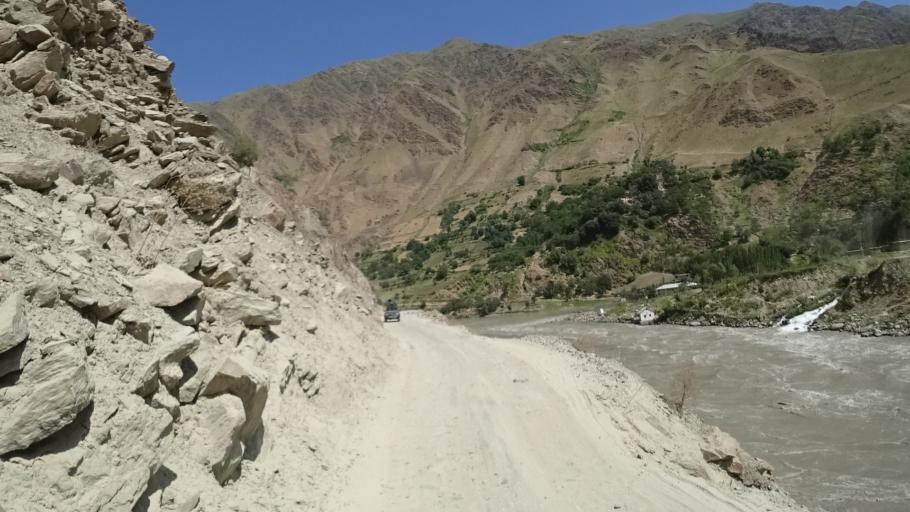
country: AF
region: Badakhshan
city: Maymay
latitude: 38.4386
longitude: 70.9507
